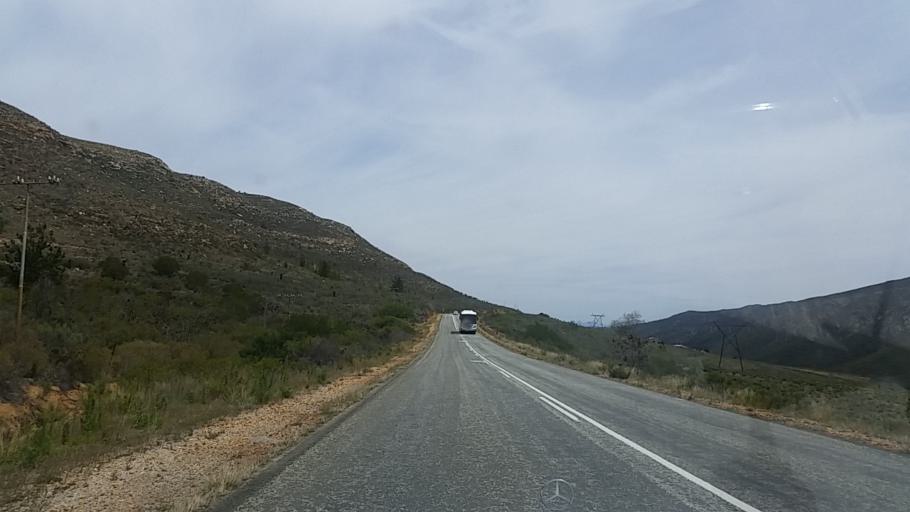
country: ZA
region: Western Cape
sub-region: Eden District Municipality
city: Knysna
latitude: -33.7452
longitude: 22.9893
